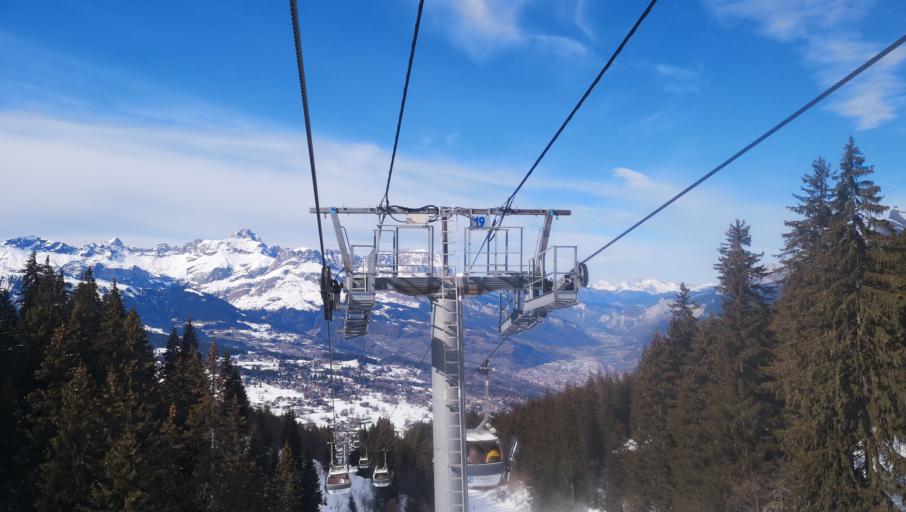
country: FR
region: Rhone-Alpes
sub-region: Departement de la Haute-Savoie
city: Combloux
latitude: 45.8637
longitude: 6.6581
